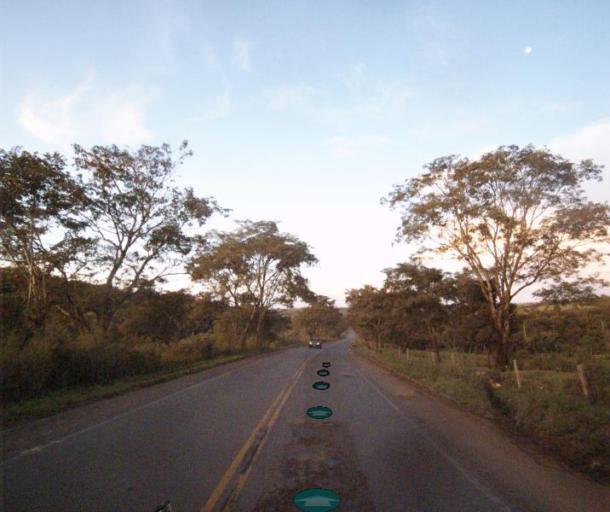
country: BR
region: Goias
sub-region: Pirenopolis
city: Pirenopolis
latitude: -15.9923
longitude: -48.8365
